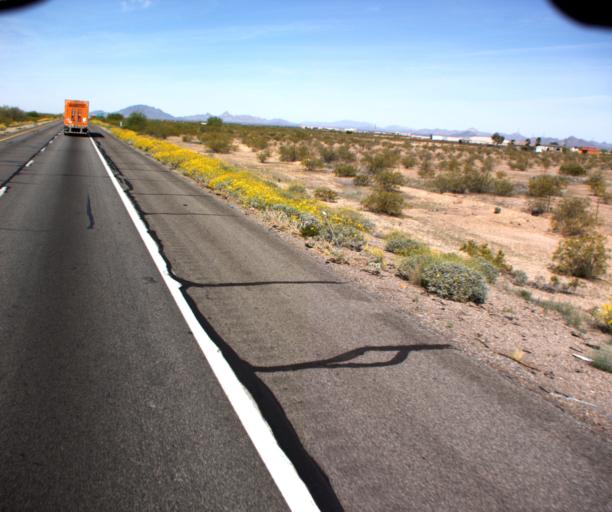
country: US
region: Arizona
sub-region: Maricopa County
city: Buckeye
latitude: 33.4791
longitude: -112.8545
